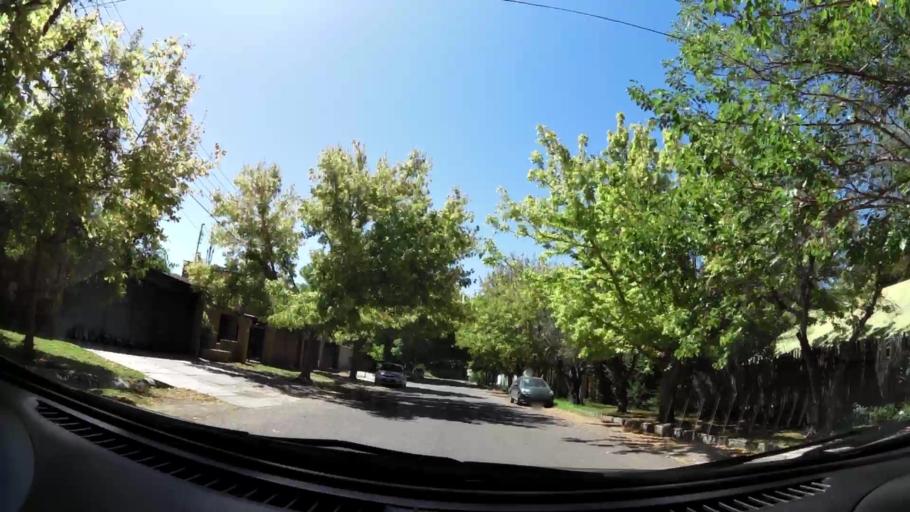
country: AR
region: Mendoza
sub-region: Departamento de Godoy Cruz
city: Godoy Cruz
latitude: -32.9680
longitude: -68.8705
